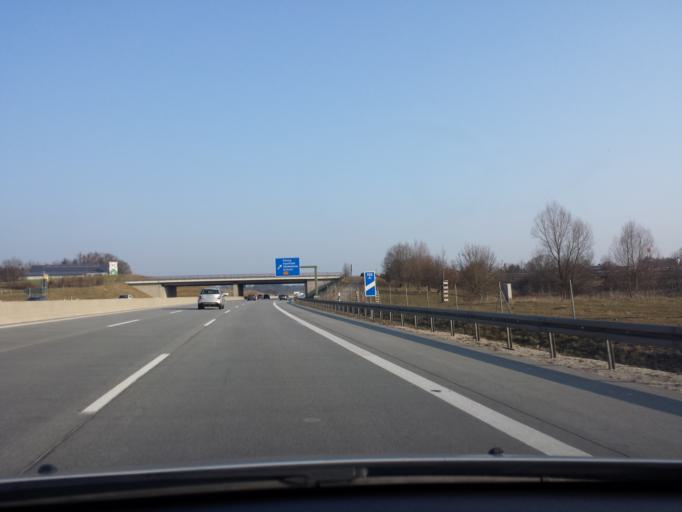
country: DE
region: Bavaria
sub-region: Swabia
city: Dasing
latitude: 48.3942
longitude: 11.0642
